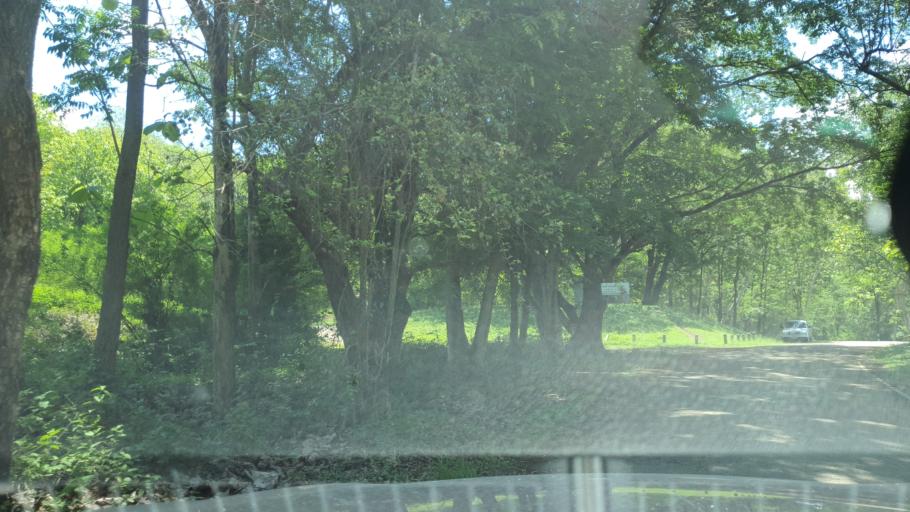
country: TH
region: Chiang Mai
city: Mae On
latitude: 18.8131
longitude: 99.2653
